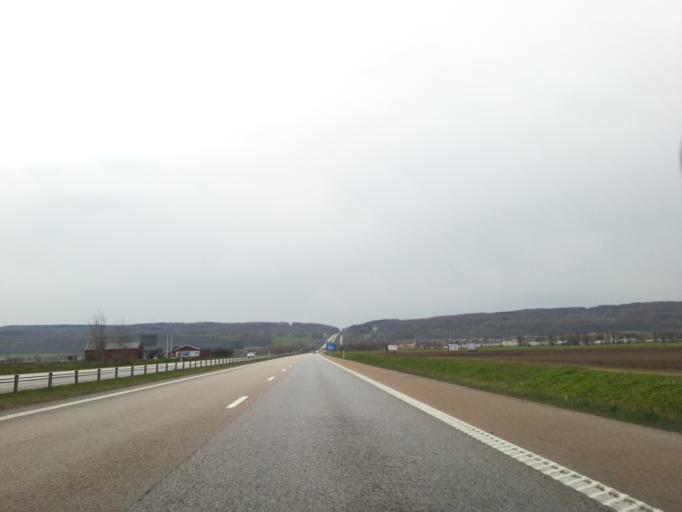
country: SE
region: Halland
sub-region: Laholms Kommun
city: Mellbystrand
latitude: 56.4380
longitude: 12.9537
